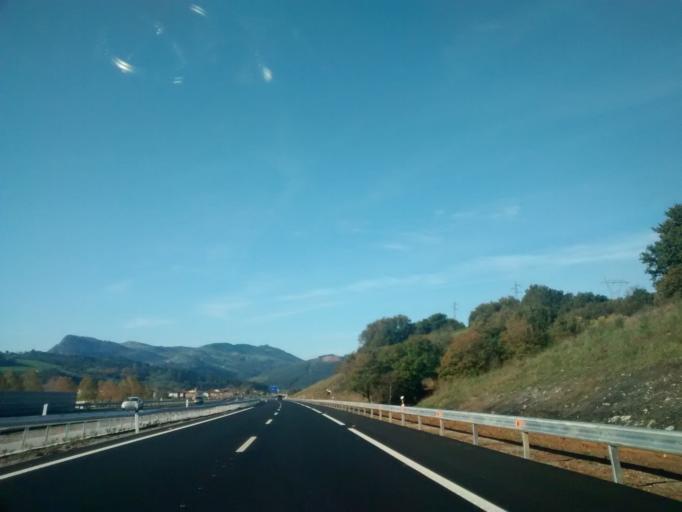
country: ES
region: Cantabria
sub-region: Provincia de Cantabria
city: Villafufre
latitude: 43.3123
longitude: -3.9175
